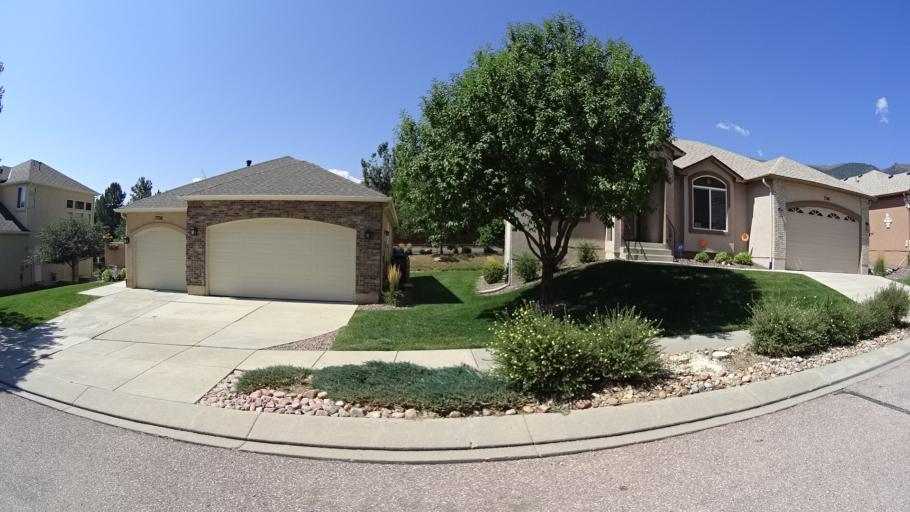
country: US
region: Colorado
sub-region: El Paso County
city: Air Force Academy
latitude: 38.9376
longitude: -104.8750
